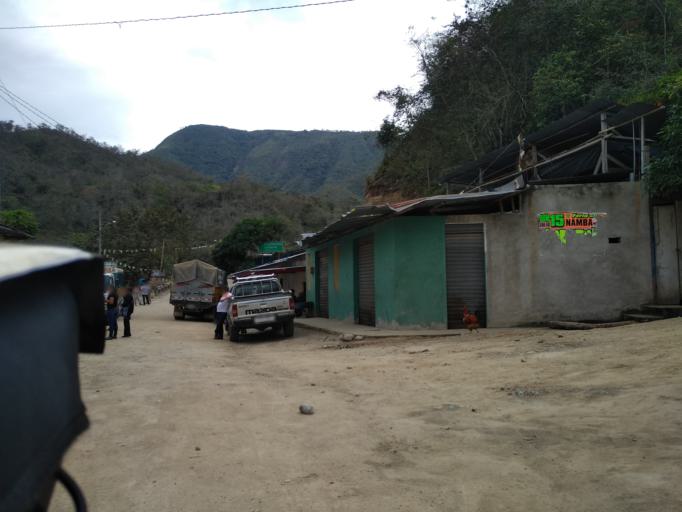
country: PE
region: Cajamarca
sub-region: Provincia de San Ignacio
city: Namballe
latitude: -4.9768
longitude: -79.1152
